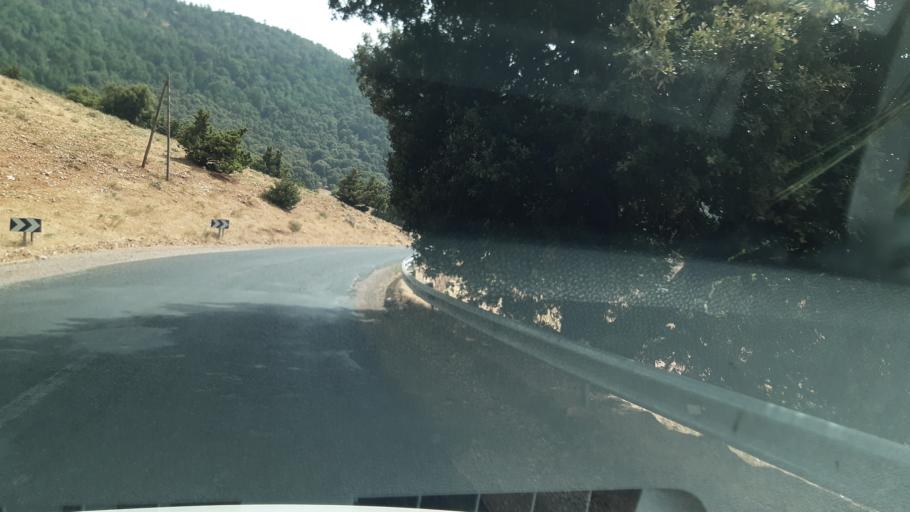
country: MA
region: Meknes-Tafilalet
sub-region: Ifrane
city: Azrou
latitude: 33.4279
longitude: -5.1906
